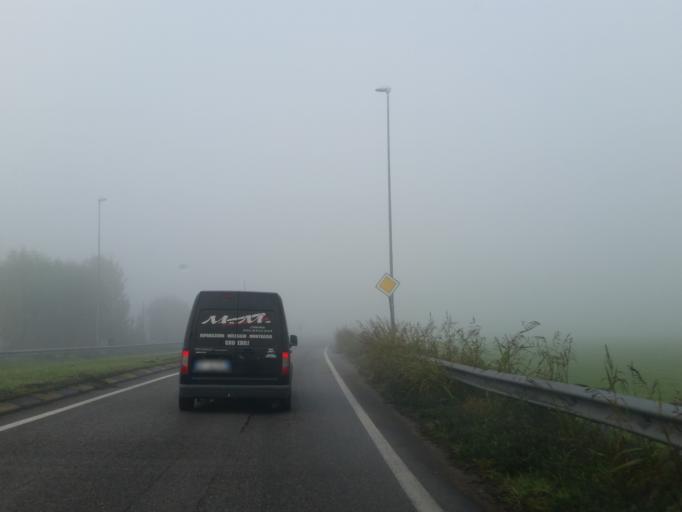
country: IT
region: Lombardy
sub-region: Provincia di Brescia
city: Pompiano
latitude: 45.3955
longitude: 9.9936
